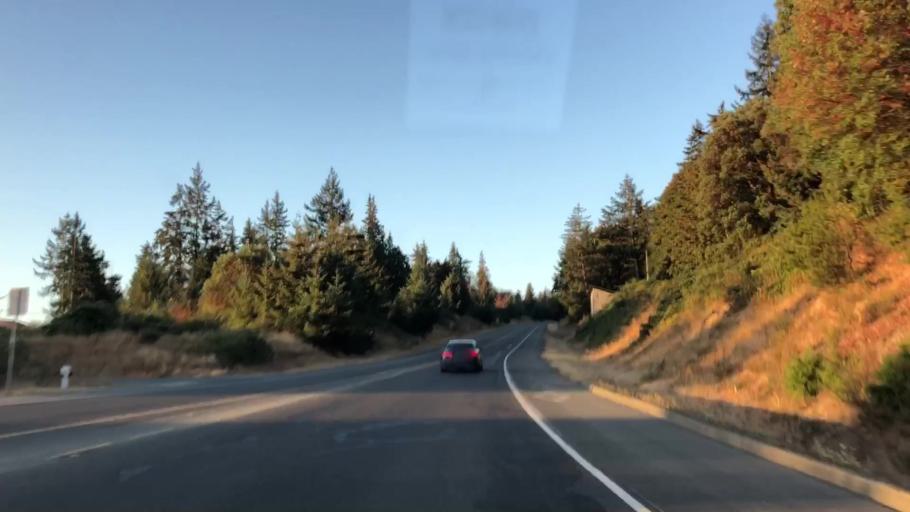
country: CA
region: British Columbia
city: Colwood
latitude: 48.4262
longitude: -123.5019
